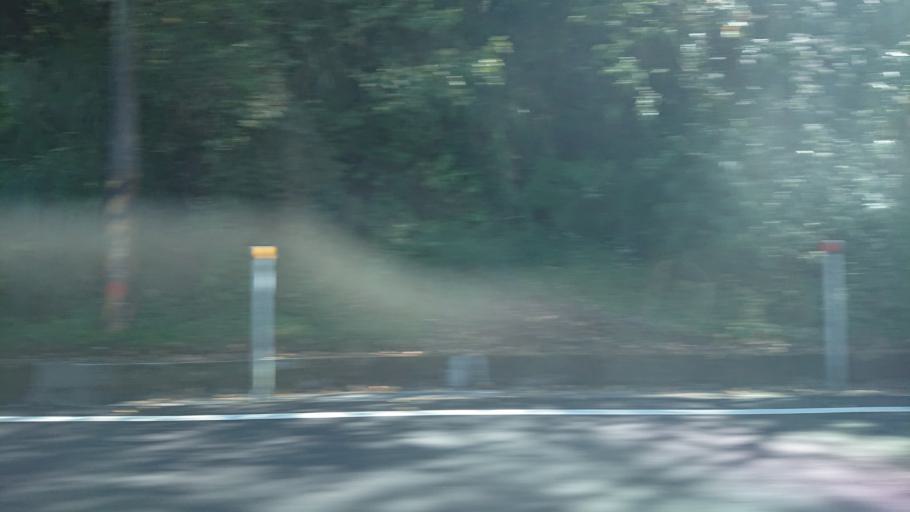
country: TW
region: Taiwan
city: Lugu
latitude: 23.4873
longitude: 120.8226
